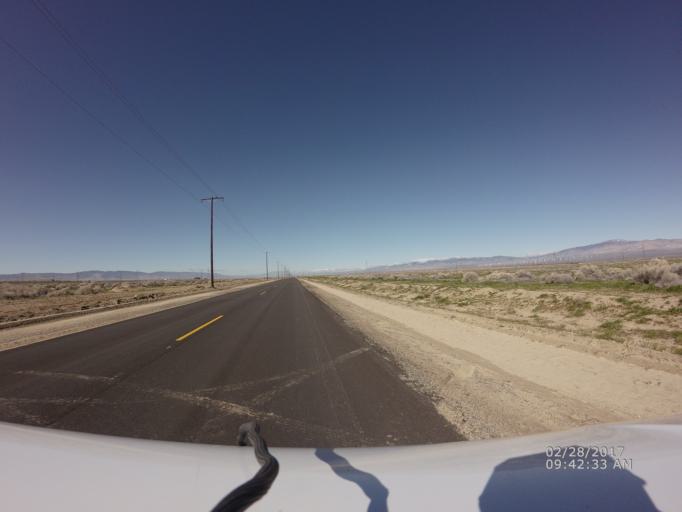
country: US
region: California
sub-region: Kern County
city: Rosamond
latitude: 34.8197
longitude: -118.3291
